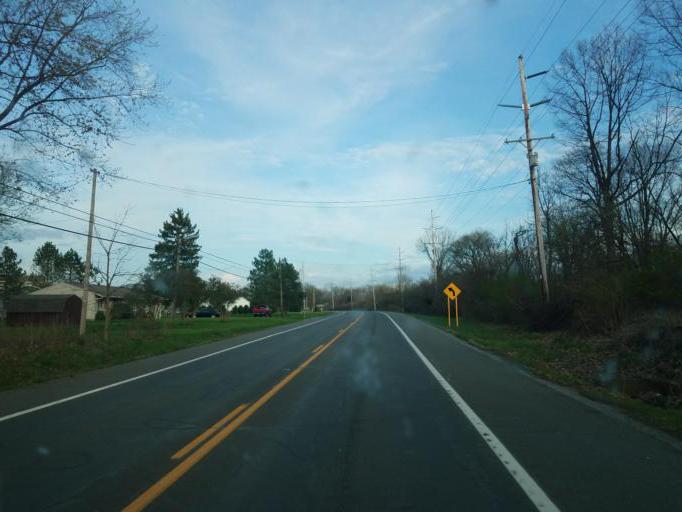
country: US
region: Ohio
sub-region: Erie County
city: Huron
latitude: 41.3814
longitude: -82.5119
